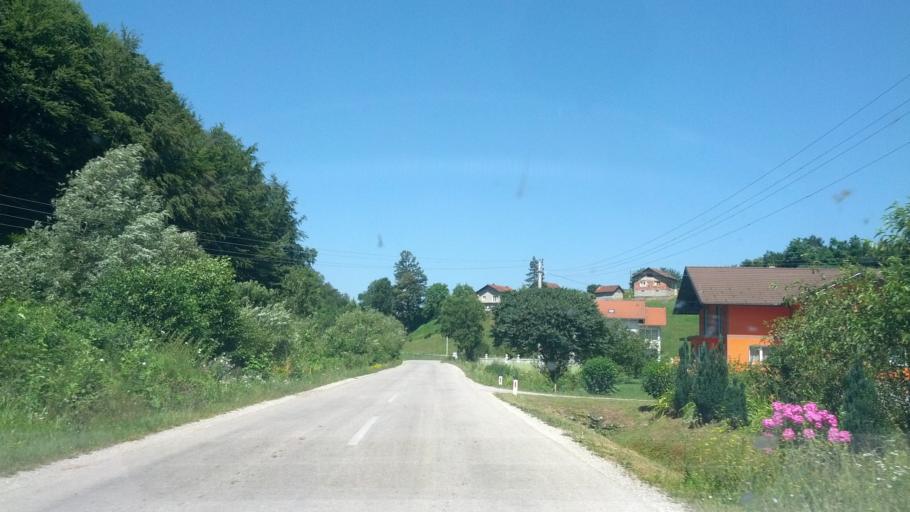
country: BA
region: Federation of Bosnia and Herzegovina
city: Otoka
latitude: 44.9918
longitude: 16.1626
